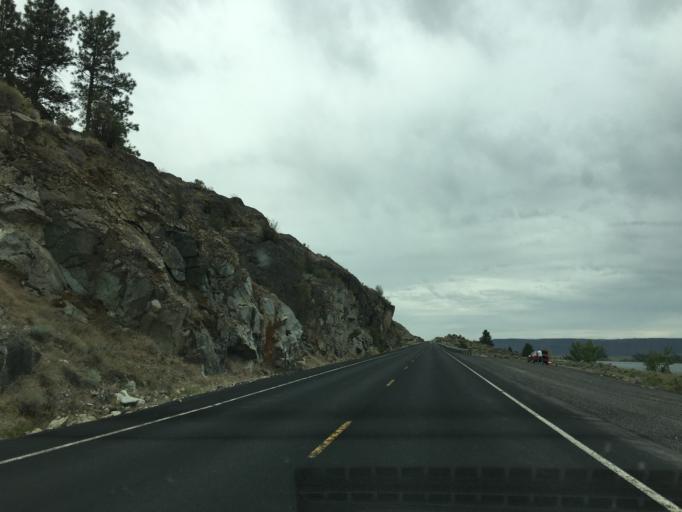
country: US
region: Washington
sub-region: Okanogan County
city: Coulee Dam
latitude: 47.8560
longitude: -119.1055
